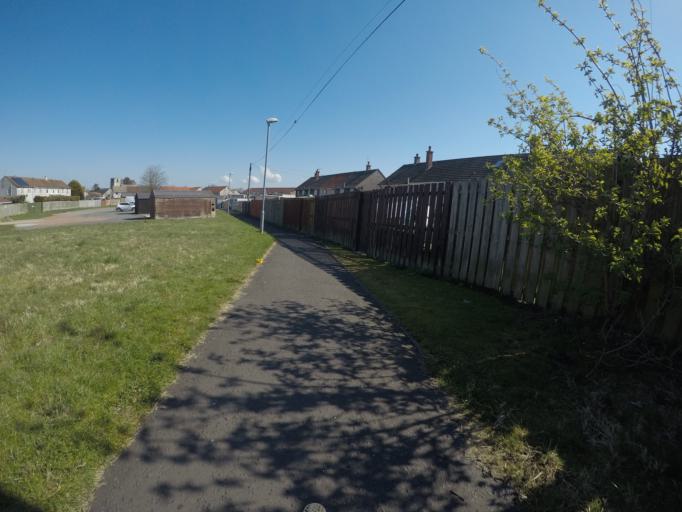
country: GB
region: Scotland
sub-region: North Ayrshire
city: Irvine
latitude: 55.6221
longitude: -4.6625
